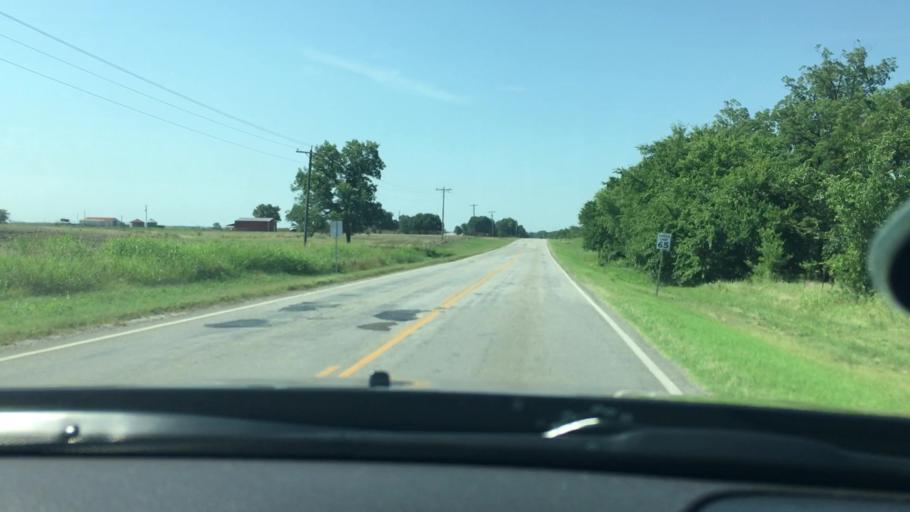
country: US
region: Oklahoma
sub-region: Coal County
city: Coalgate
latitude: 34.3626
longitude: -96.4246
